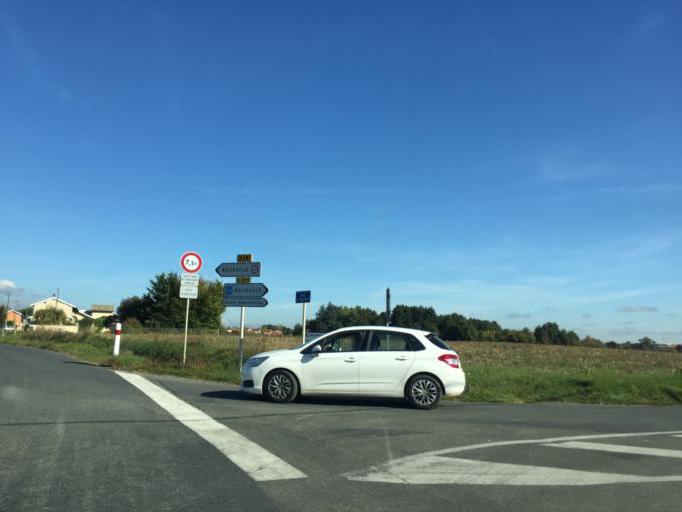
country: FR
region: Rhone-Alpes
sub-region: Departement du Rhone
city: Belleville
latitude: 46.1016
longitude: 4.7191
